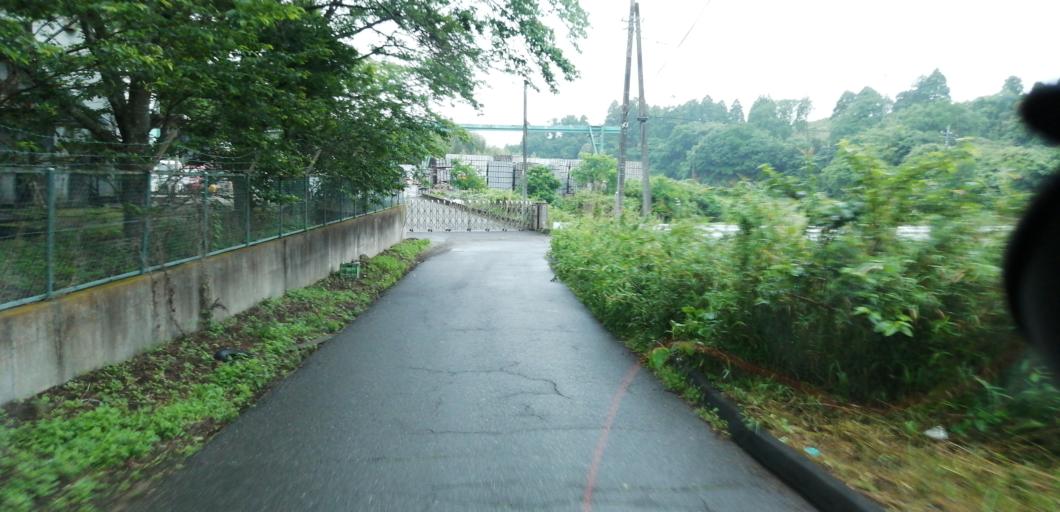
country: JP
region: Chiba
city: Yachimata
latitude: 35.5905
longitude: 140.2717
